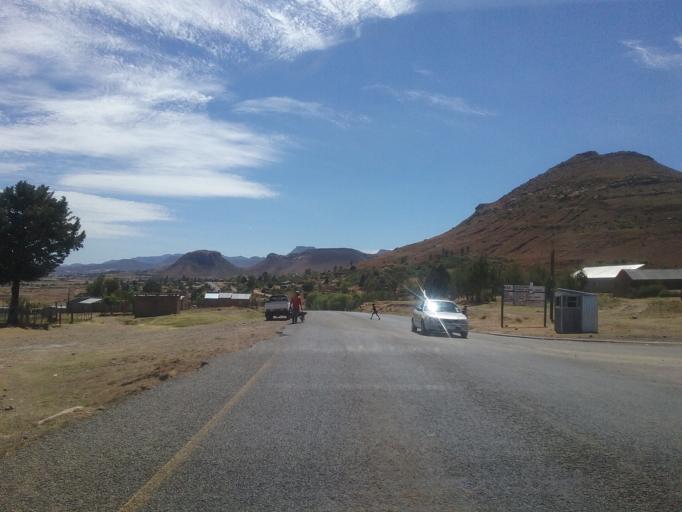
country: LS
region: Mohale's Hoek District
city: Mohale's Hoek
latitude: -30.1869
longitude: 27.4201
